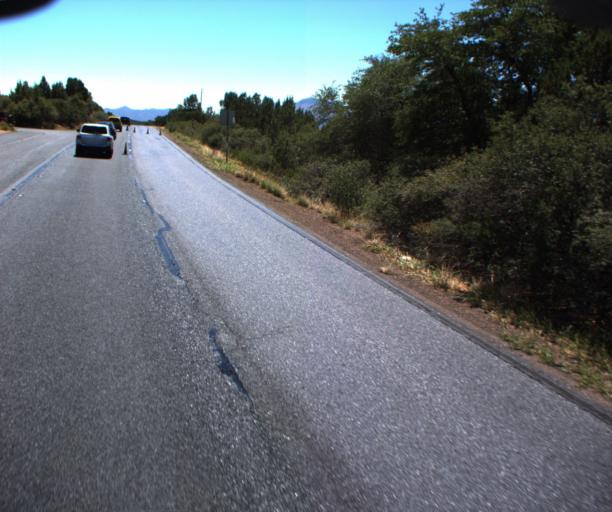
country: US
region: Arizona
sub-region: Gila County
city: Payson
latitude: 34.1931
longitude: -111.3293
